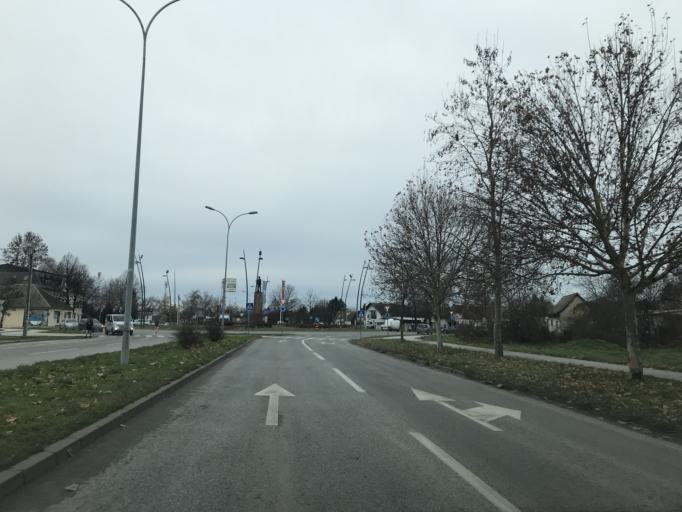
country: RS
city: Veternik
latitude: 45.2493
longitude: 19.7574
